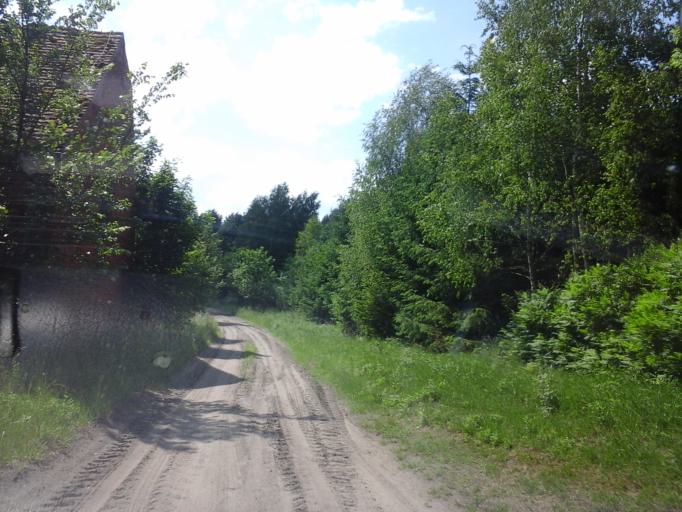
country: PL
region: West Pomeranian Voivodeship
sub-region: Powiat choszczenski
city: Bierzwnik
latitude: 53.0880
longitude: 15.7154
